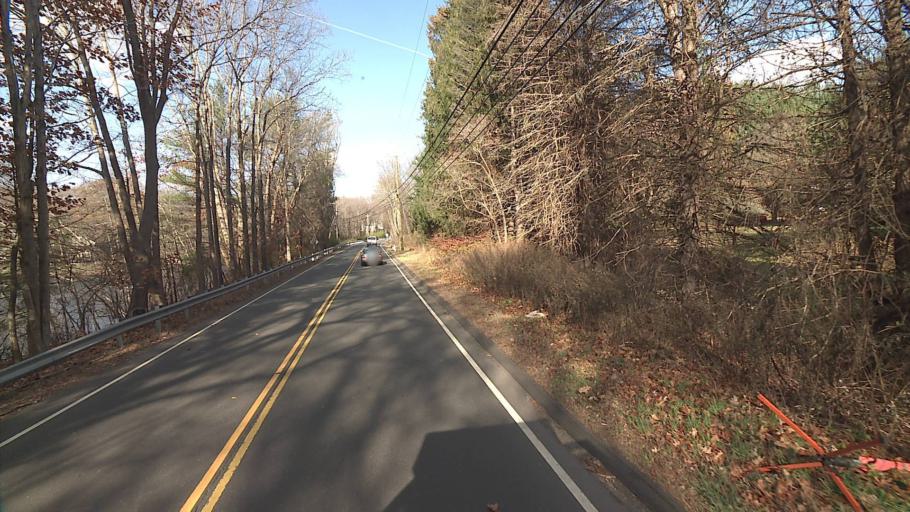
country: US
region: Connecticut
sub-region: Fairfield County
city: Wilton
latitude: 41.2208
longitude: -73.3837
